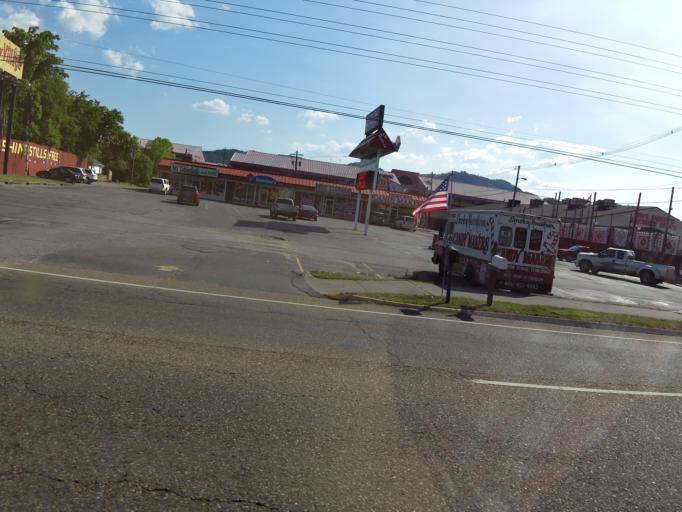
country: US
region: Tennessee
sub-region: Sevier County
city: Pigeon Forge
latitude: 35.7974
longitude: -83.5668
